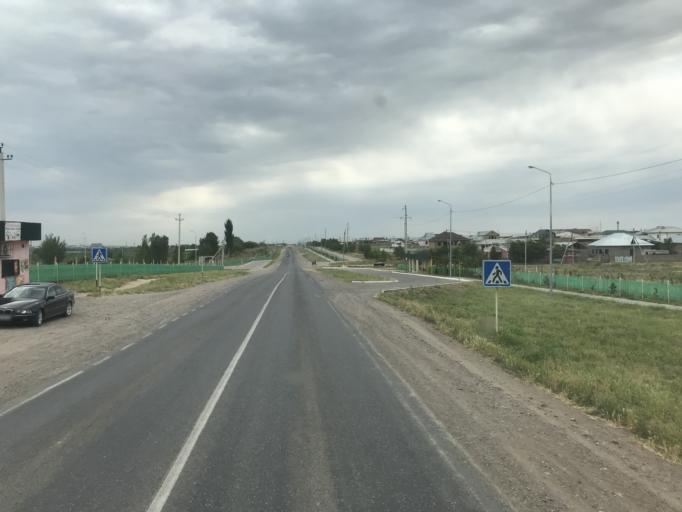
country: KZ
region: Ongtustik Qazaqstan
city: Saryaghash
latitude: 41.4215
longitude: 69.0907
